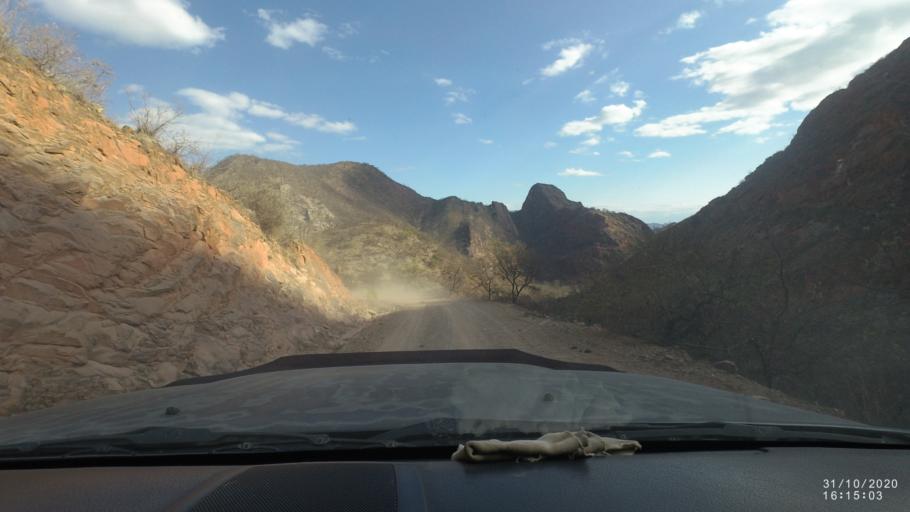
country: BO
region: Chuquisaca
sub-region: Provincia Zudanez
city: Mojocoya
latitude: -18.3870
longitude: -64.6142
